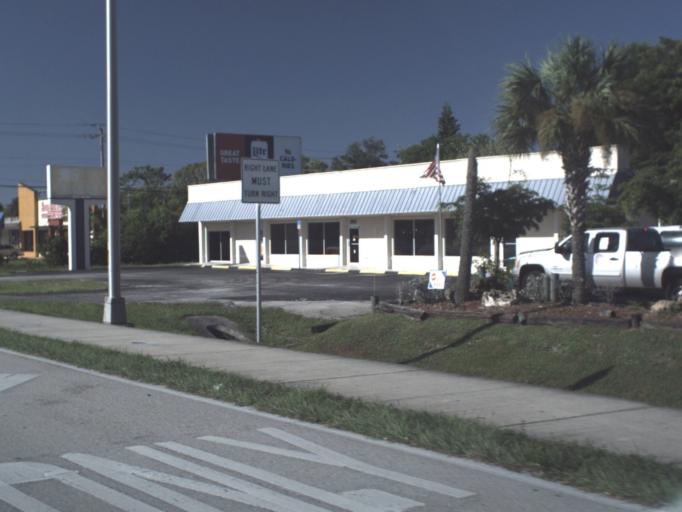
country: US
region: Florida
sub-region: Lee County
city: Pine Manor
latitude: 26.5761
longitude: -81.8720
